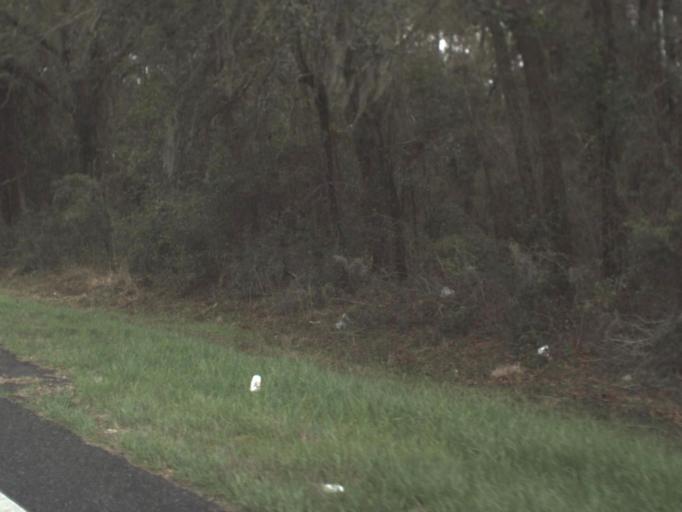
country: US
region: Florida
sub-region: Gadsden County
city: Havana
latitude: 30.5477
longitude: -84.3760
